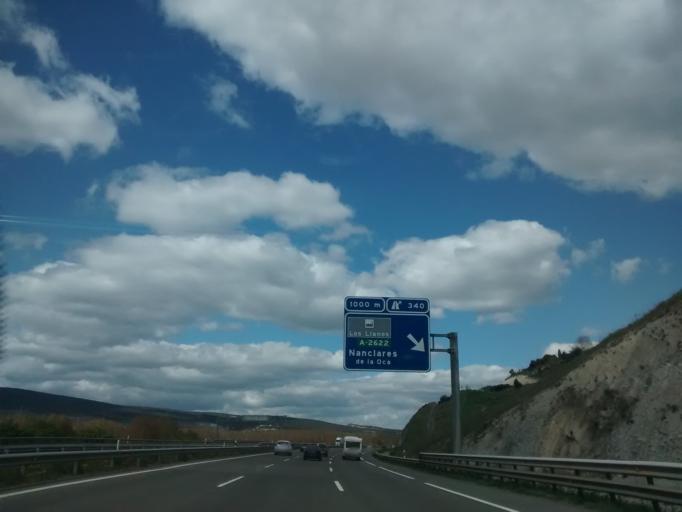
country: ES
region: Basque Country
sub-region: Provincia de Alava
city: Arminon
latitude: 42.7956
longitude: -2.8203
